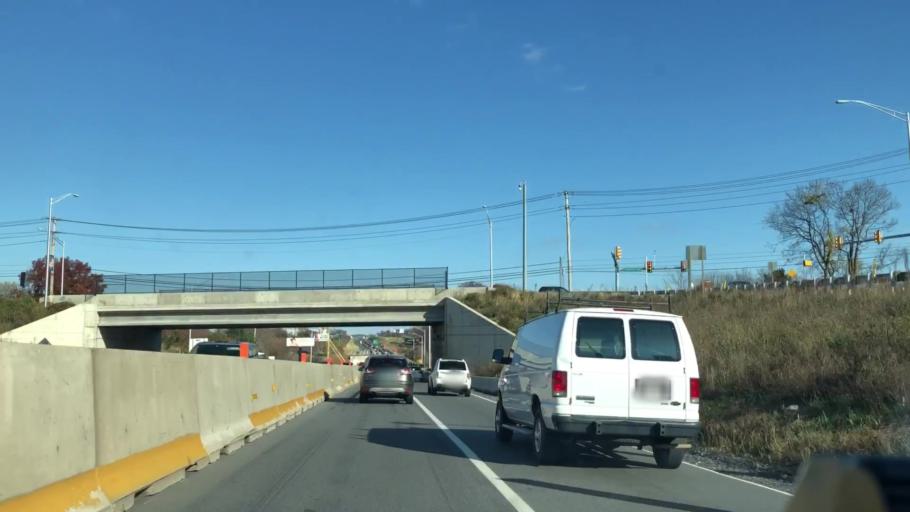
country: US
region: Pennsylvania
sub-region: Lehigh County
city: Fullerton
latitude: 40.6305
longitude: -75.4710
